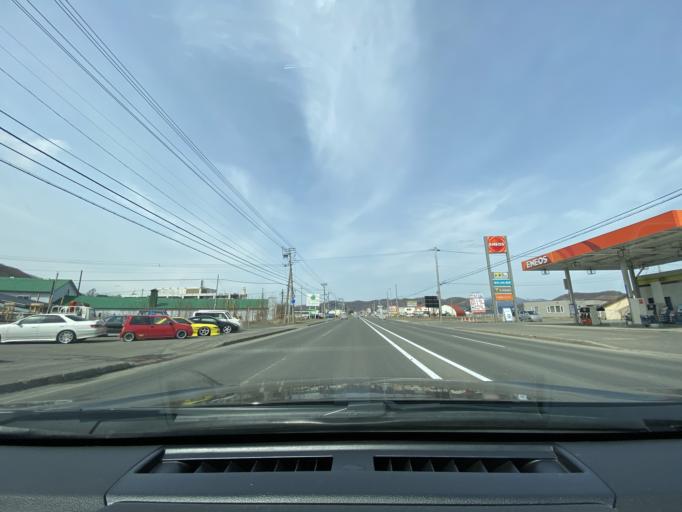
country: JP
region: Hokkaido
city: Kitami
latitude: 43.8020
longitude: 143.8189
